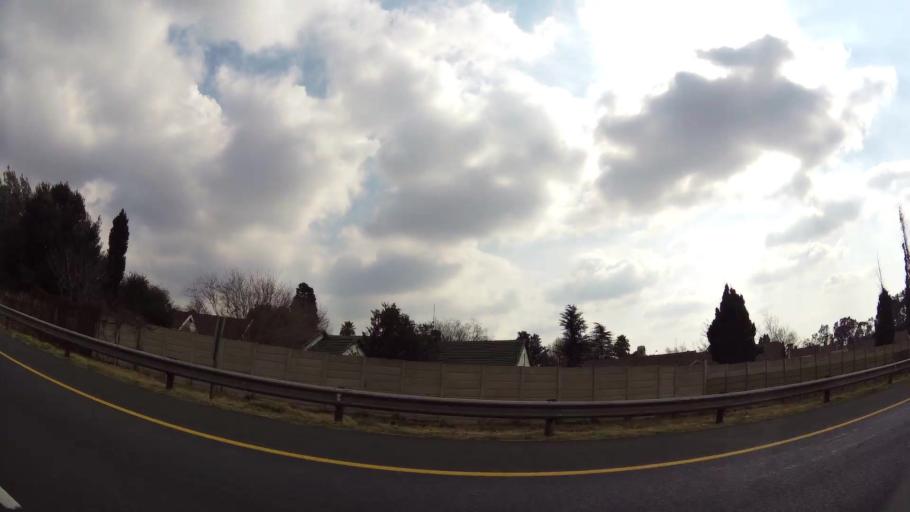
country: ZA
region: Gauteng
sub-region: Ekurhuleni Metropolitan Municipality
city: Benoni
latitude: -26.1638
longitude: 28.3588
